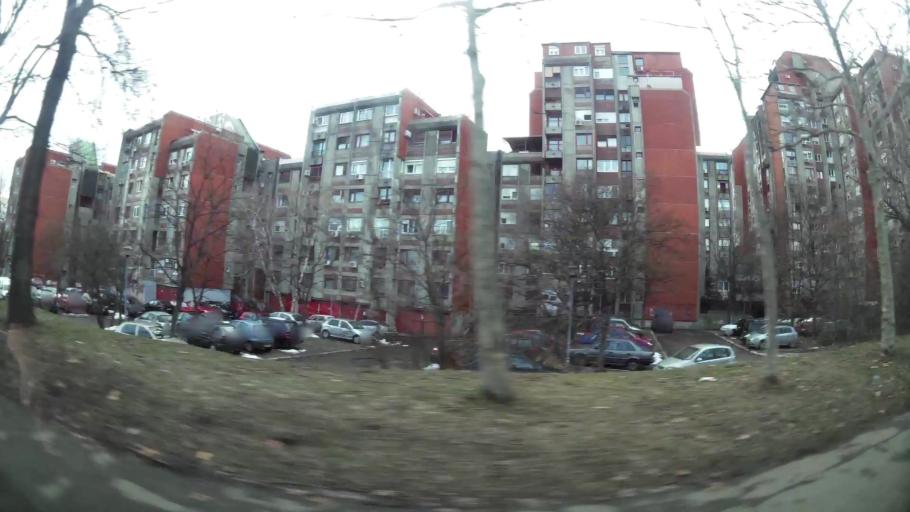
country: RS
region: Central Serbia
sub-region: Belgrade
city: Vozdovac
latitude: 44.7579
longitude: 20.4824
